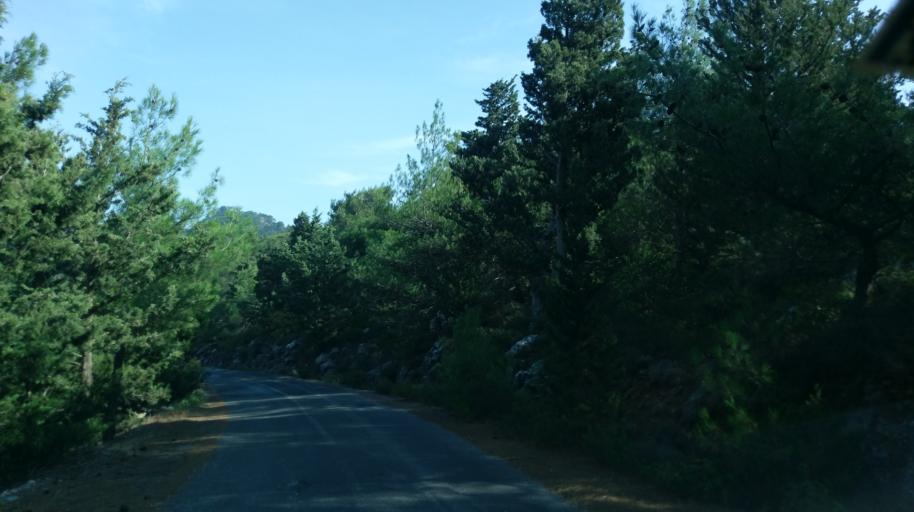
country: CY
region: Keryneia
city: Kyrenia
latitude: 35.3043
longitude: 33.2644
